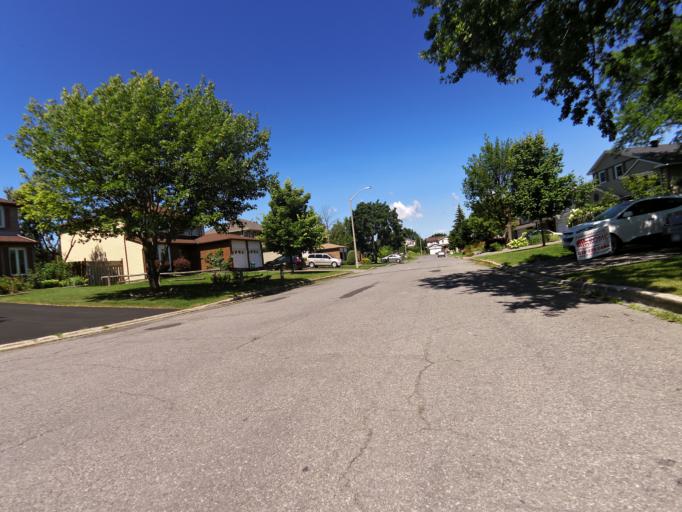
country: CA
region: Ontario
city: Ottawa
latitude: 45.3487
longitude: -75.6607
